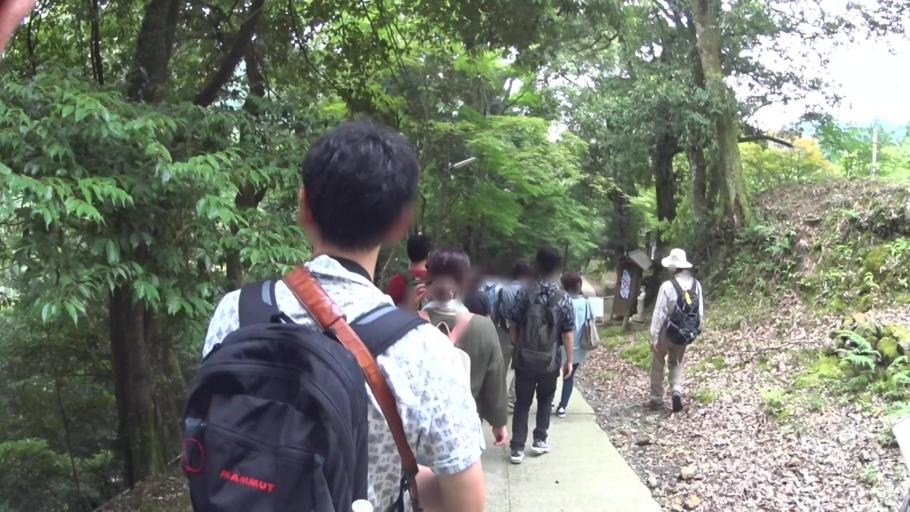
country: JP
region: Kyoto
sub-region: Kyoto-shi
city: Kamigyo-ku
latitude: 35.0546
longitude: 135.6726
